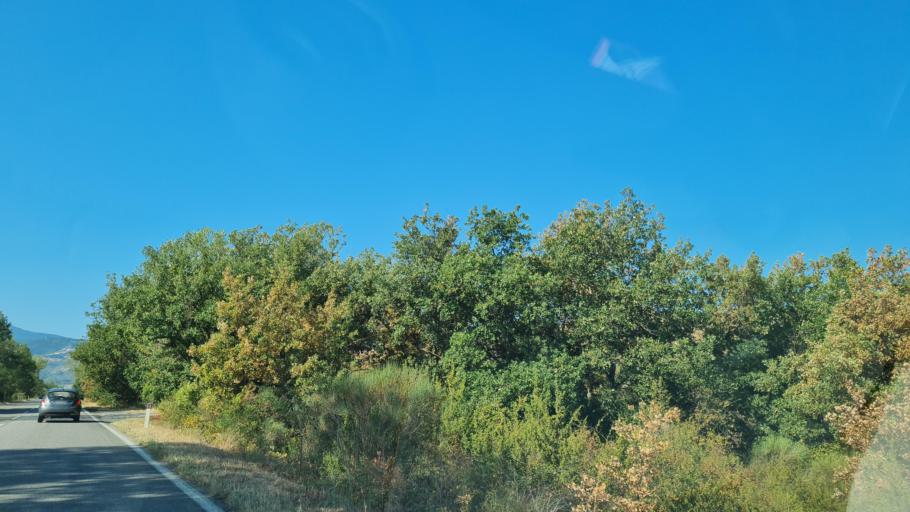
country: IT
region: Tuscany
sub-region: Provincia di Siena
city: Pienza
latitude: 42.9937
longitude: 11.7215
